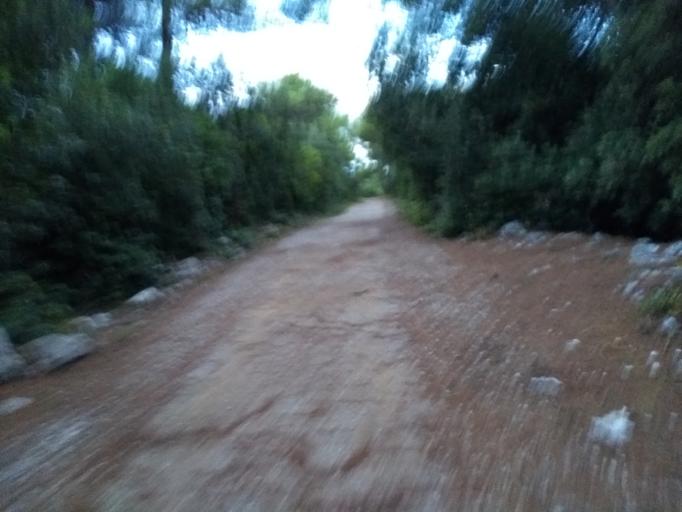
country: HR
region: Zadarska
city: Ugljan
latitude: 44.1335
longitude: 15.0693
